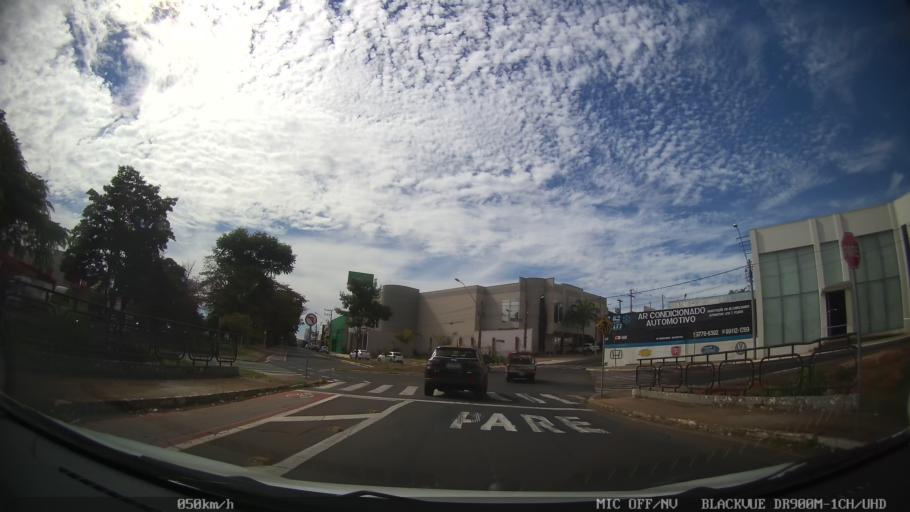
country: BR
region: Sao Paulo
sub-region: Catanduva
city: Catanduva
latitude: -21.1471
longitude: -48.9744
